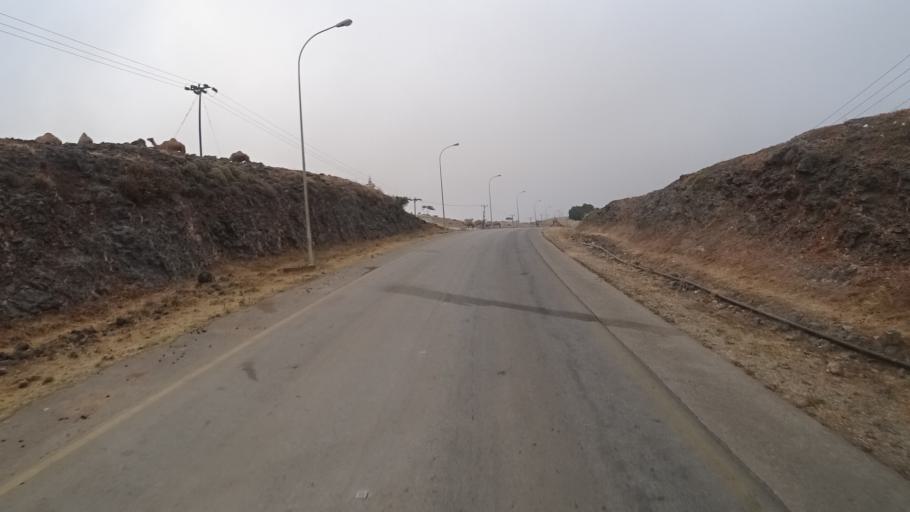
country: OM
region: Zufar
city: Salalah
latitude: 17.1235
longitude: 53.9758
